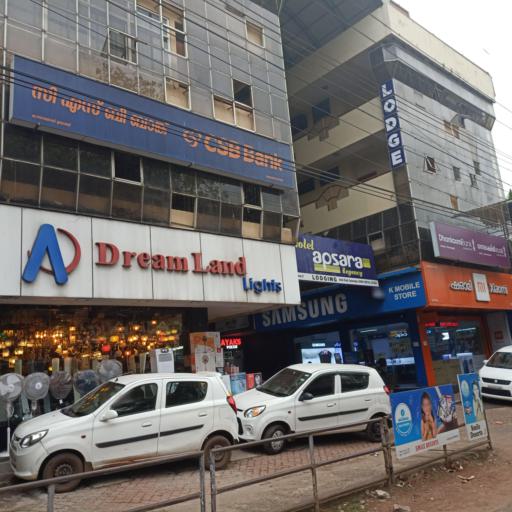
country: IN
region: Kerala
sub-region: Kasaragod District
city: Kasaragod
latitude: 12.5027
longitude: 74.9875
